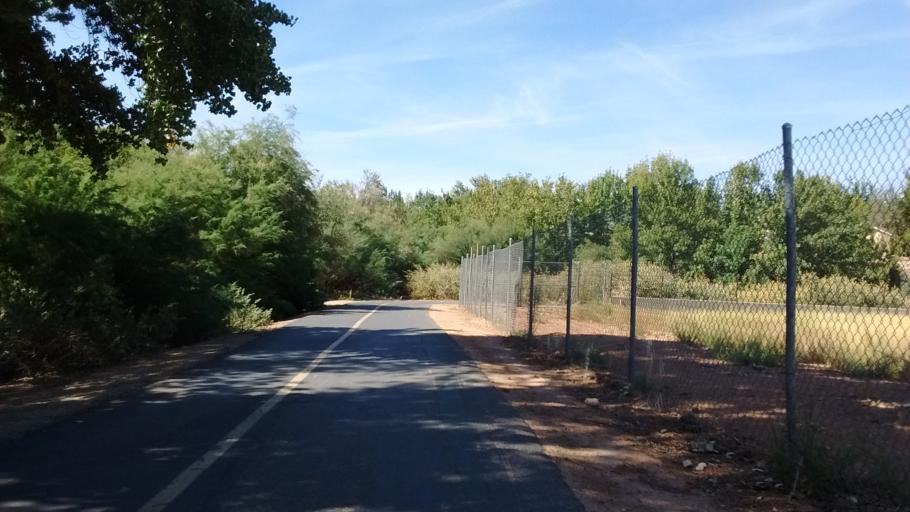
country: US
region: Utah
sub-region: Washington County
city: Saint George
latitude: 37.0870
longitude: -113.5540
